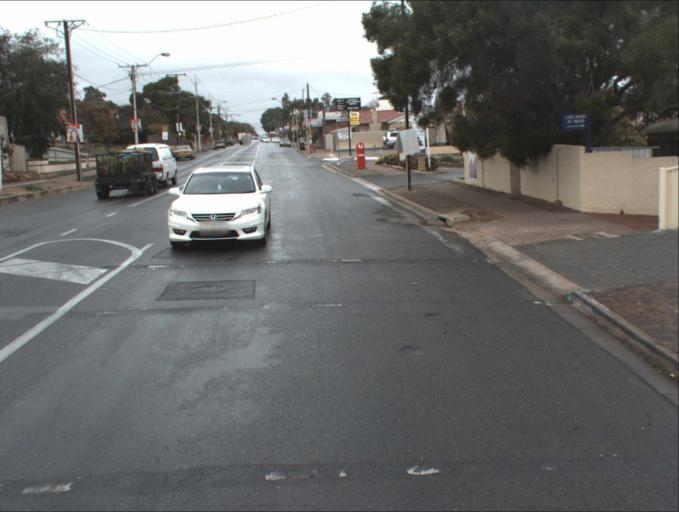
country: AU
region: South Australia
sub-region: Port Adelaide Enfield
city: Blair Athol
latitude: -34.8700
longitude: 138.5929
